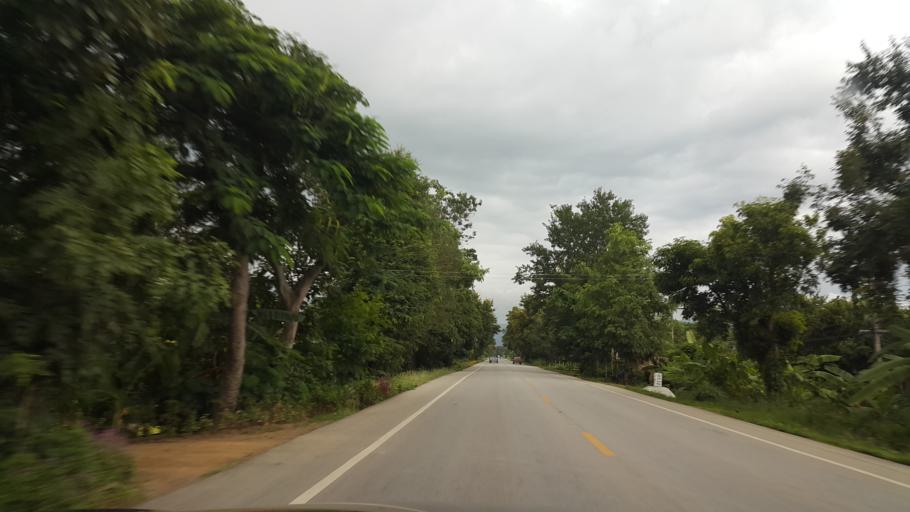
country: TH
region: Phayao
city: Dok Kham Tai
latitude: 19.1924
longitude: 100.0244
